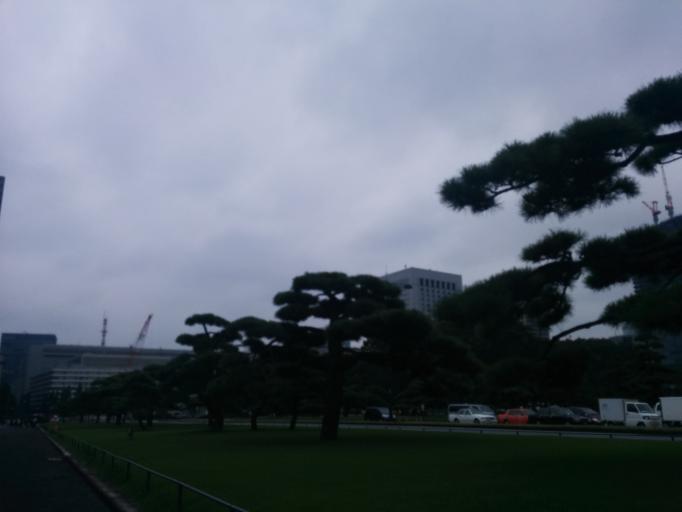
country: JP
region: Tokyo
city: Tokyo
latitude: 35.6796
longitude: 139.7581
